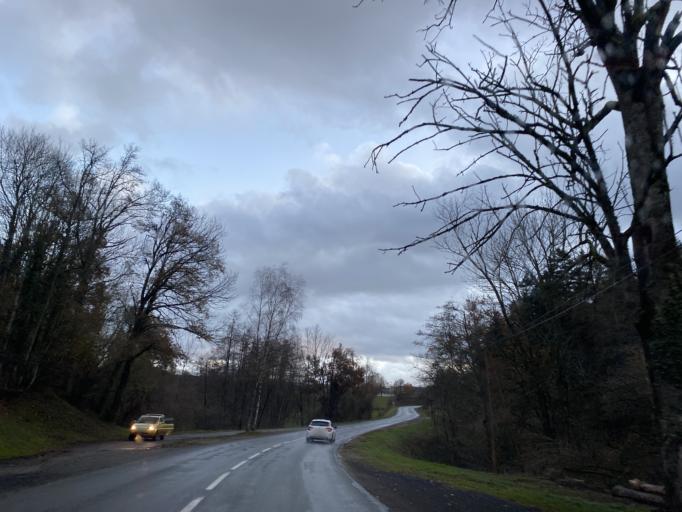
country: FR
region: Auvergne
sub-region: Departement du Puy-de-Dome
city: Cunlhat
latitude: 45.6465
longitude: 3.5596
